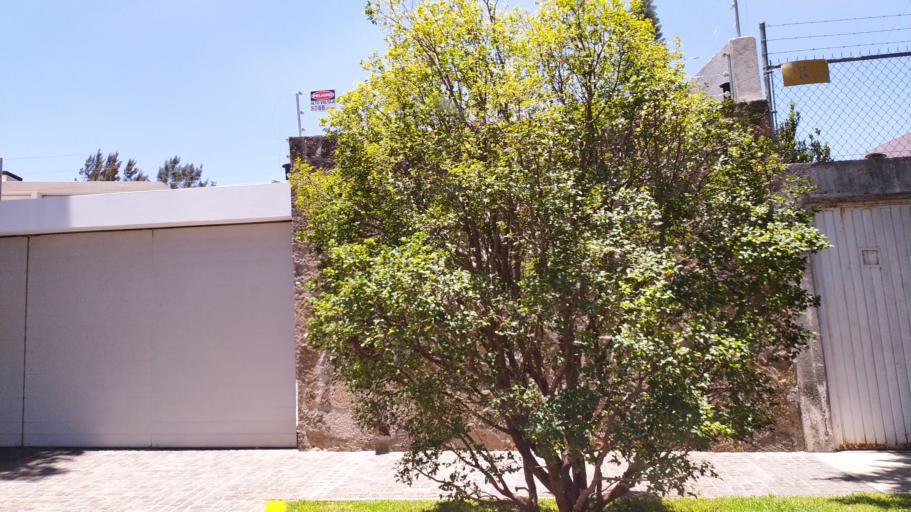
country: MX
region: Jalisco
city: Guadalajara
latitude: 20.6884
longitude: -103.4071
